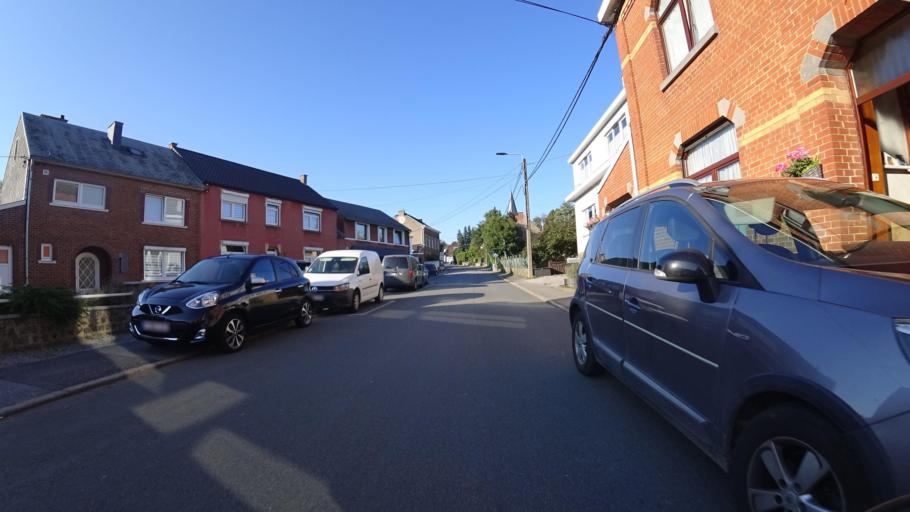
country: BE
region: Wallonia
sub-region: Province de Namur
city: Namur
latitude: 50.4909
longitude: 4.8471
